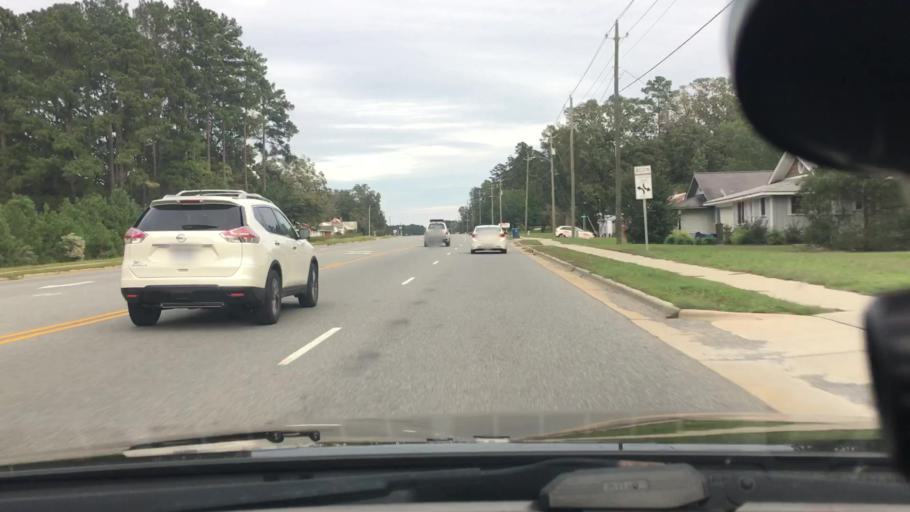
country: US
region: North Carolina
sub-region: Montgomery County
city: Biscoe
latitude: 35.3599
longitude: -79.7762
